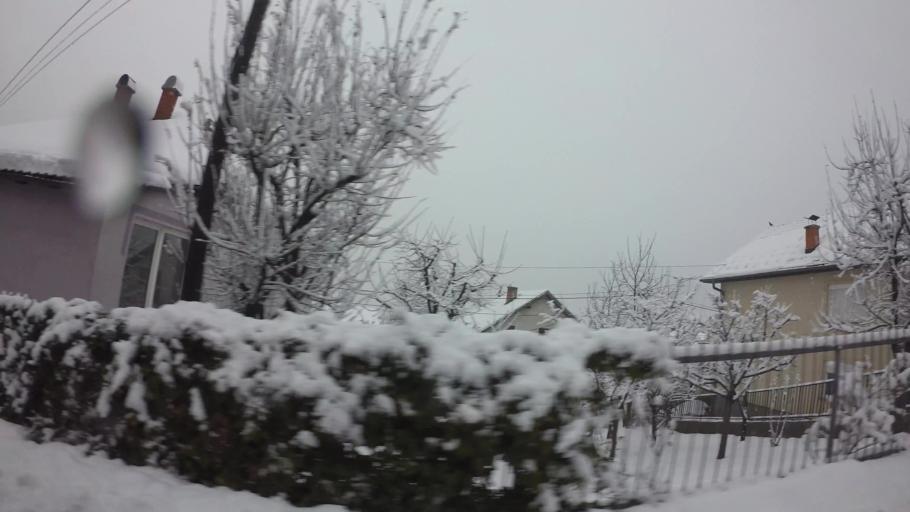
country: BA
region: Federation of Bosnia and Herzegovina
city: Vogosca
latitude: 43.8693
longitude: 18.3185
